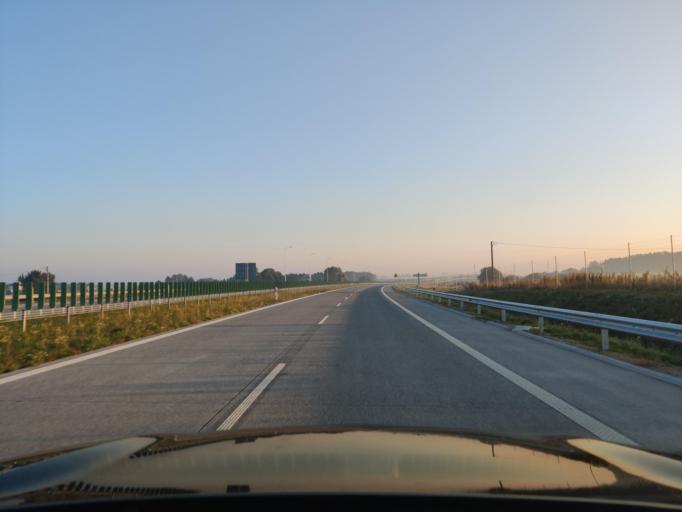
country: PL
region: Masovian Voivodeship
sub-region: Powiat mlawski
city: Wisniewo
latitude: 53.0670
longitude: 20.3689
